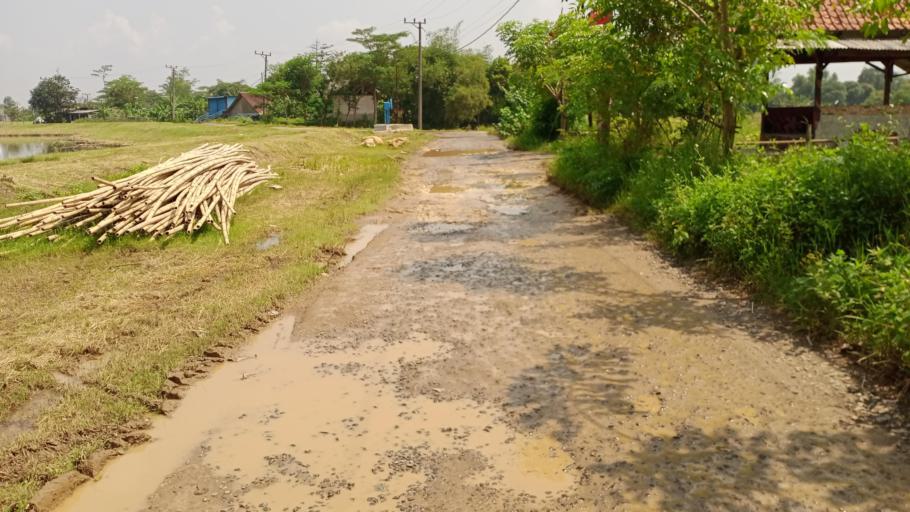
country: ID
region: West Java
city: Cileungsir
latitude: -6.4074
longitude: 107.1025
